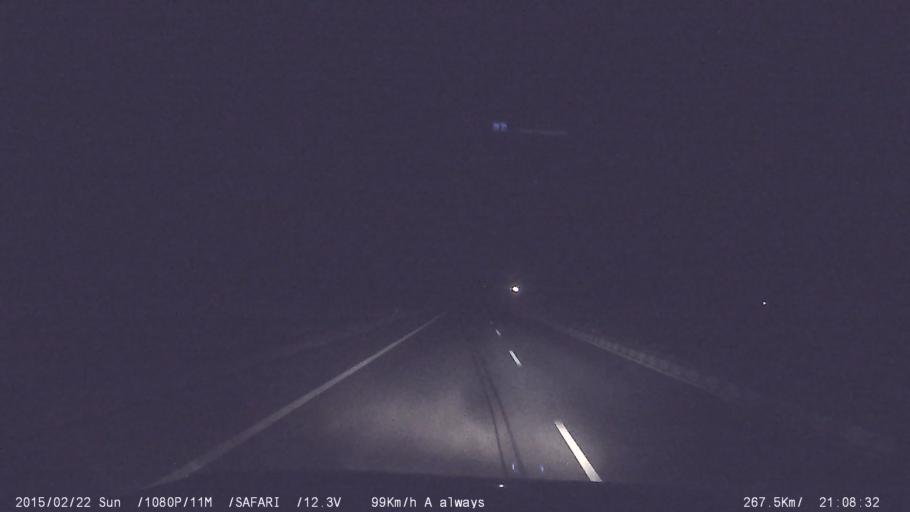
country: IN
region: Tamil Nadu
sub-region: Karur
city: Pallappatti
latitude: 10.7353
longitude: 77.9217
